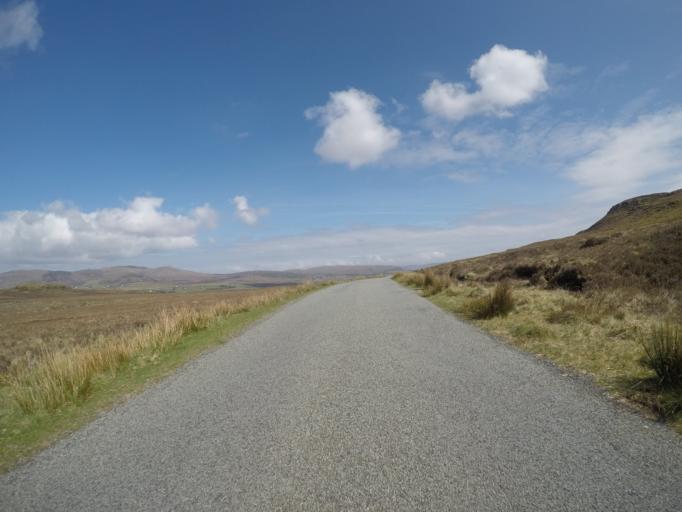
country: GB
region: Scotland
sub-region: Highland
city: Isle of Skye
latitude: 57.4227
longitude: -6.2771
